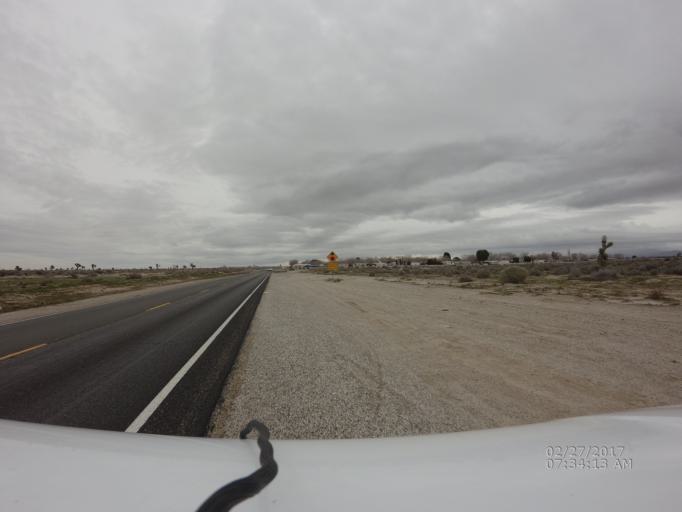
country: US
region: California
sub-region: Los Angeles County
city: Lancaster
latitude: 34.7188
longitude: -118.1145
